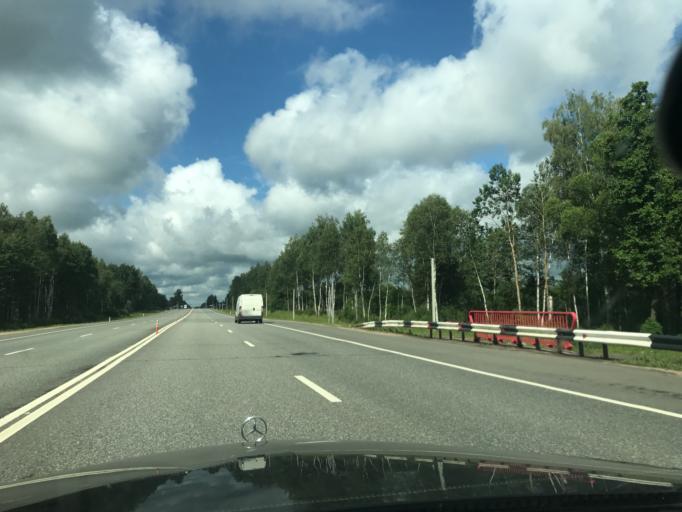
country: RU
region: Smolensk
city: Golynki
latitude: 54.7434
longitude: 31.4186
